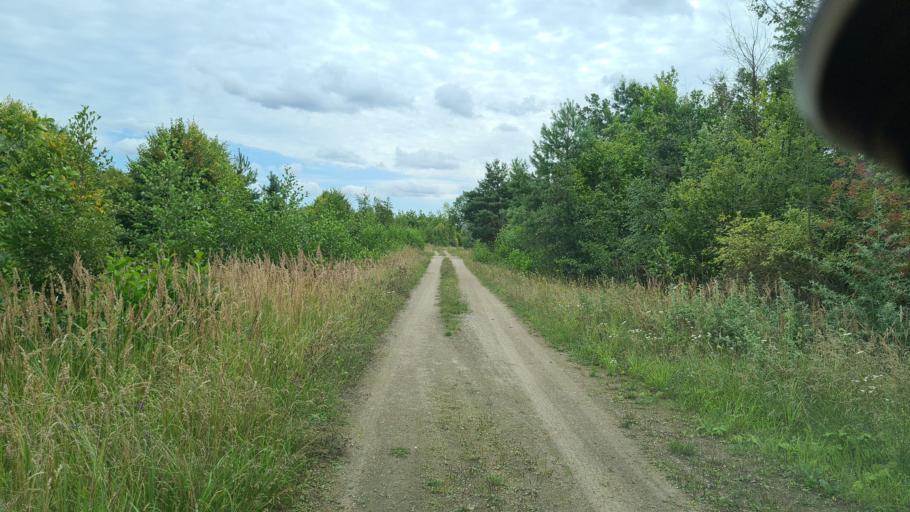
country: DE
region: Brandenburg
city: Spremberg
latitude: 51.5821
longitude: 14.3083
